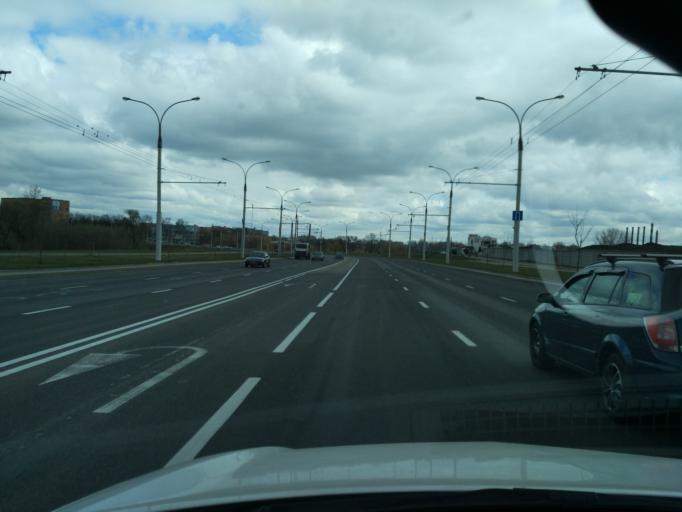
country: BY
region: Minsk
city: Yubilyeyny
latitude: 53.8544
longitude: 27.4951
